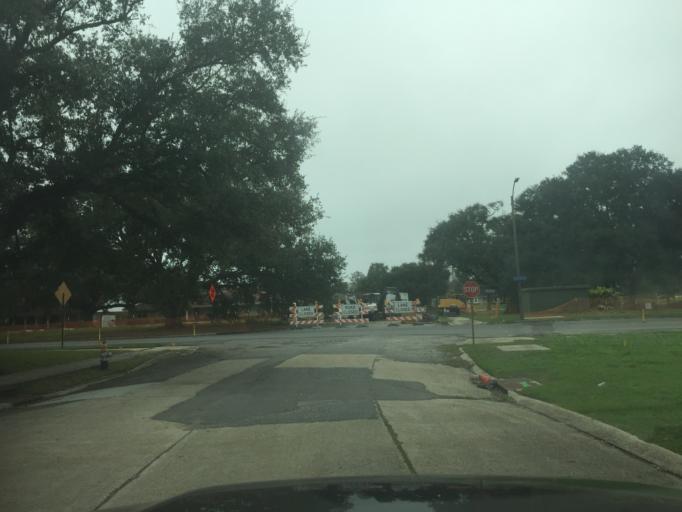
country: US
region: Louisiana
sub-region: Jefferson Parish
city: Metairie
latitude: 30.0205
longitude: -90.1067
